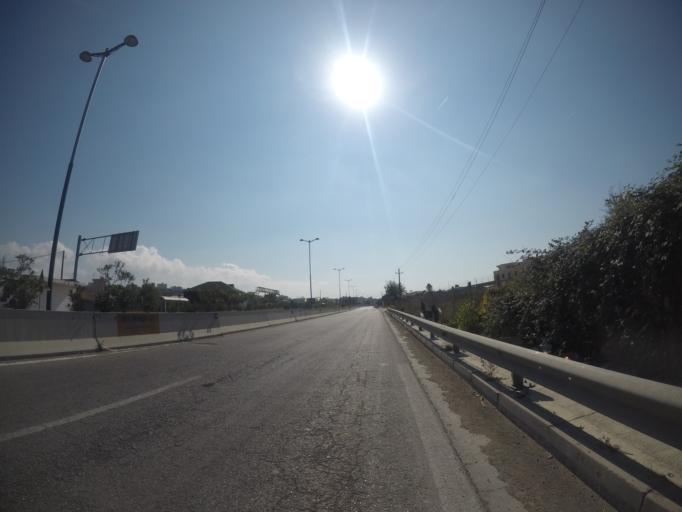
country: AL
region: Durres
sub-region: Rrethi i Durresit
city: Rrashbull
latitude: 41.3115
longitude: 19.4998
